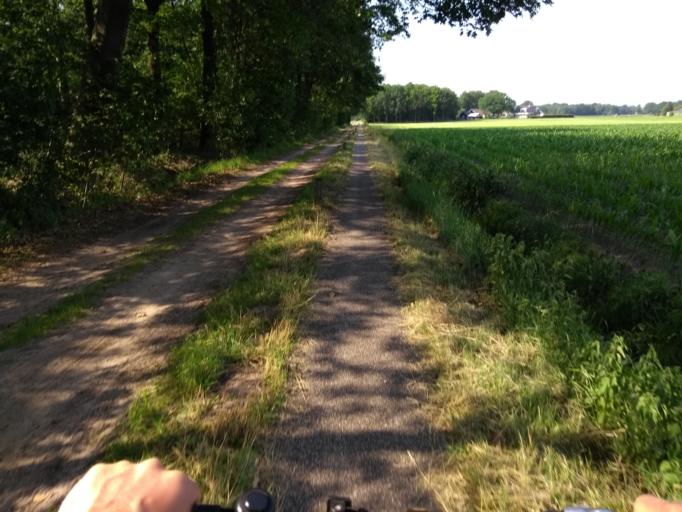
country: NL
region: Overijssel
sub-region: Gemeente Borne
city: Borne
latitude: 52.3534
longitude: 6.7270
